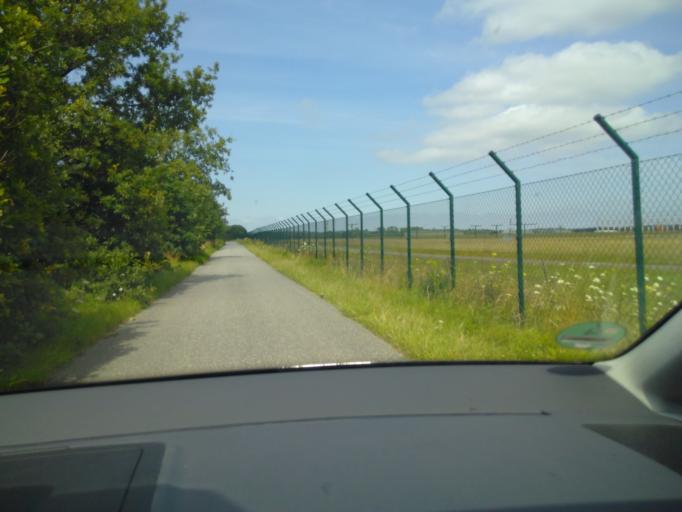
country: DE
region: Lower Saxony
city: Midlum
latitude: 53.7634
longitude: 8.6300
